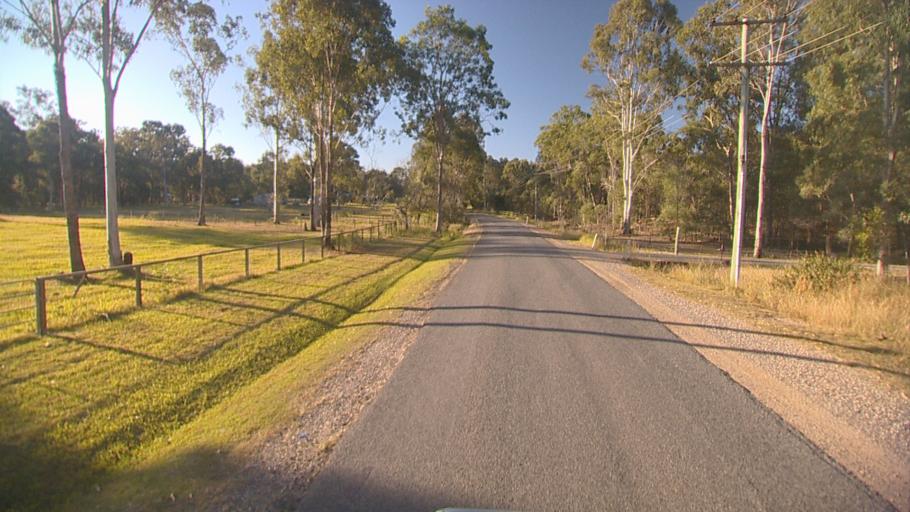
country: AU
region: Queensland
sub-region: Logan
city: Chambers Flat
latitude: -27.7771
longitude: 153.1283
